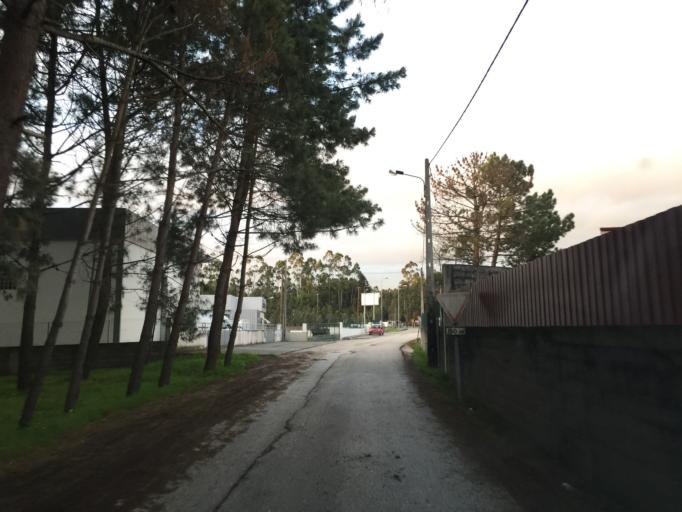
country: PT
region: Leiria
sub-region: Pombal
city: Lourical
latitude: 39.9903
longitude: -8.8031
